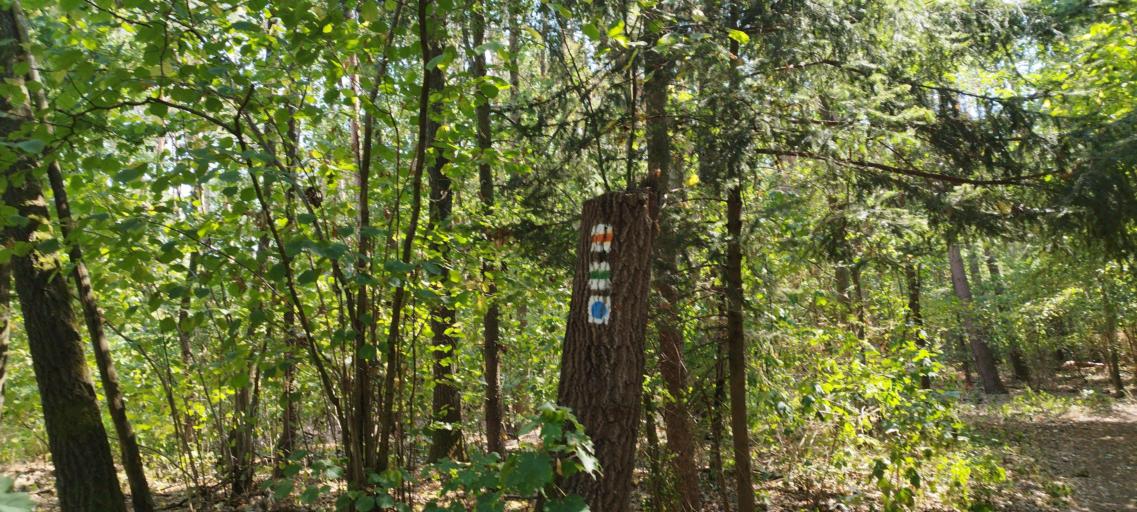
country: DE
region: Brandenburg
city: Strausberg
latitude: 52.5527
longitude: 13.8822
